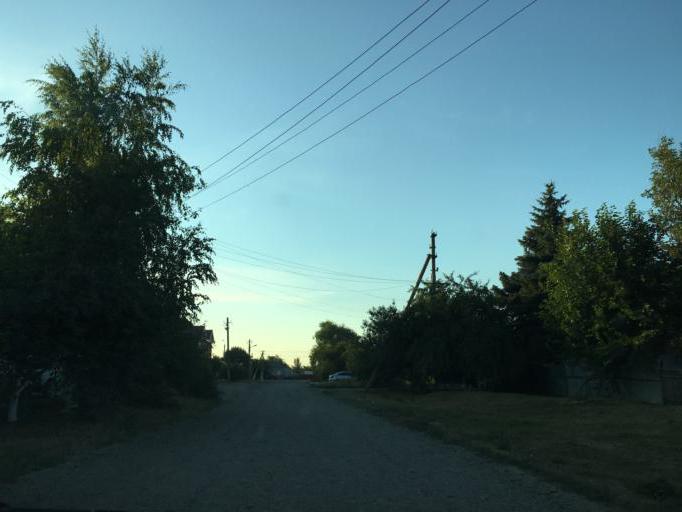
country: RU
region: Krasnodarskiy
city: Kushchevskaya
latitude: 46.5676
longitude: 39.6487
